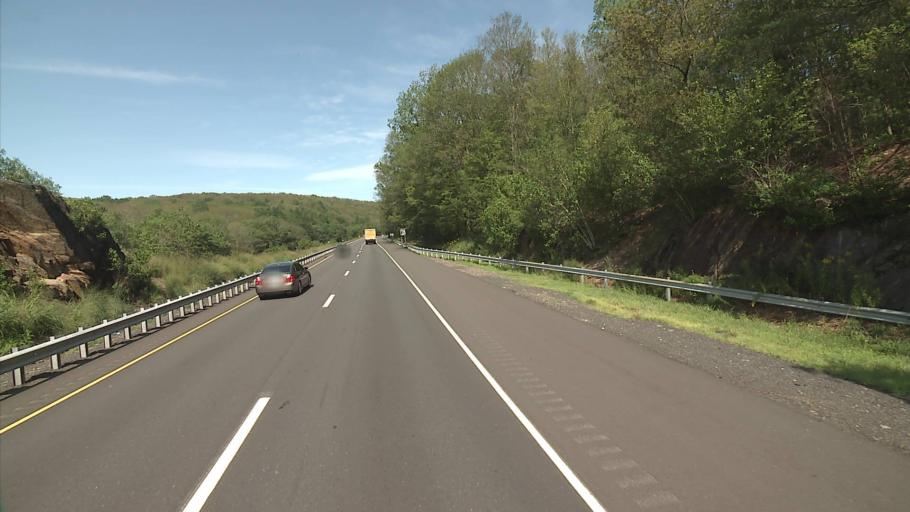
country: US
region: Connecticut
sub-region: Hartford County
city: Terramuggus
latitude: 41.6511
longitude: -72.4942
